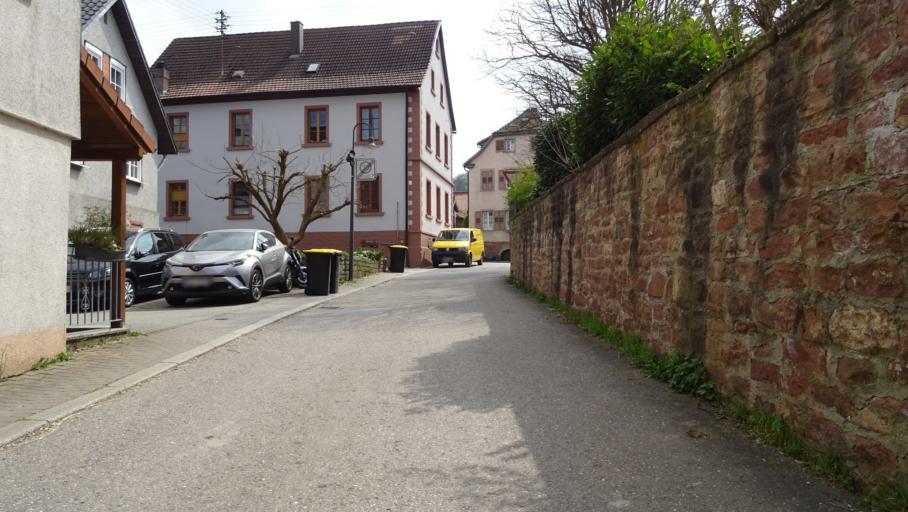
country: DE
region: Baden-Wuerttemberg
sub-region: Karlsruhe Region
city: Mosbach
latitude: 49.3778
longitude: 9.1680
